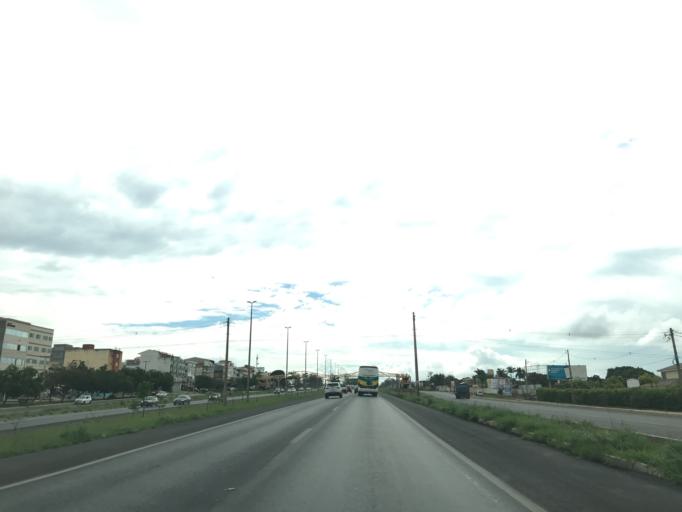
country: BR
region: Federal District
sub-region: Brasilia
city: Brasilia
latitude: -15.6798
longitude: -47.8320
